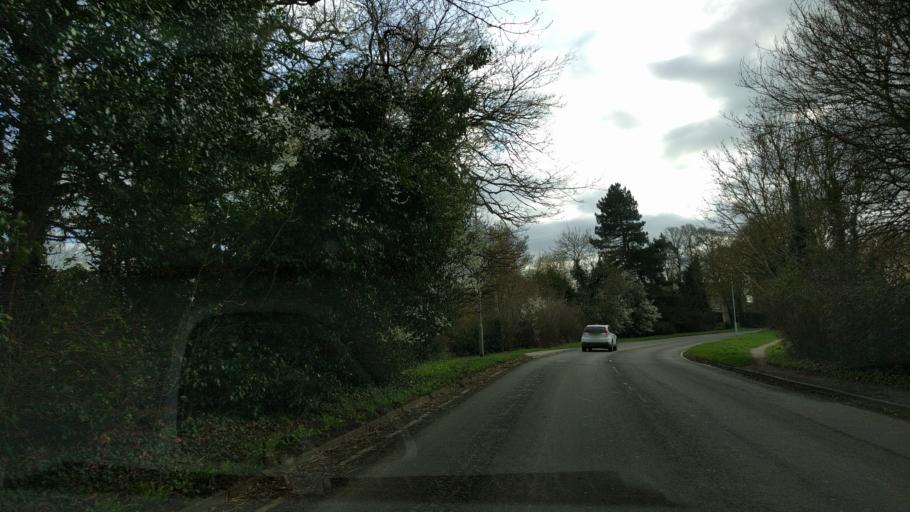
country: GB
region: England
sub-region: Cambridgeshire
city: Warboys
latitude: 52.4005
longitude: -0.0864
